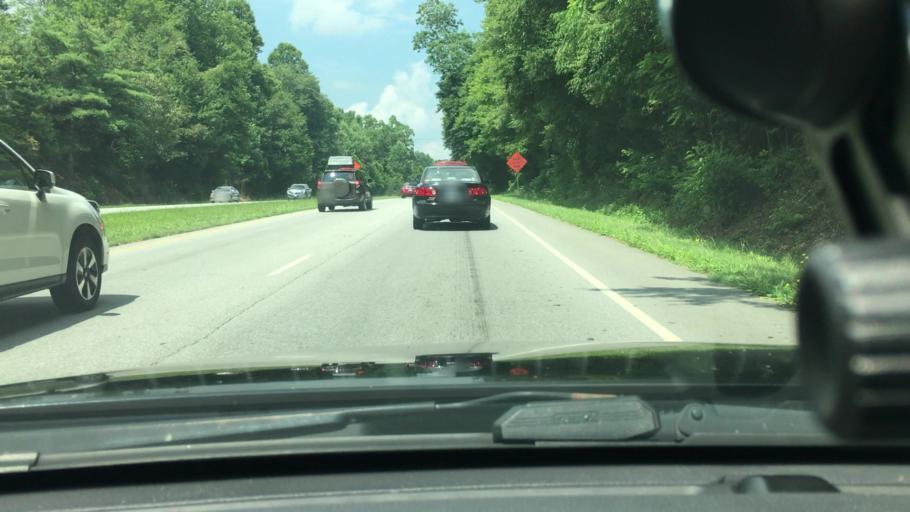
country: US
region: North Carolina
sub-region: Transylvania County
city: Brevard
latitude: 35.2658
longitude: -82.7139
